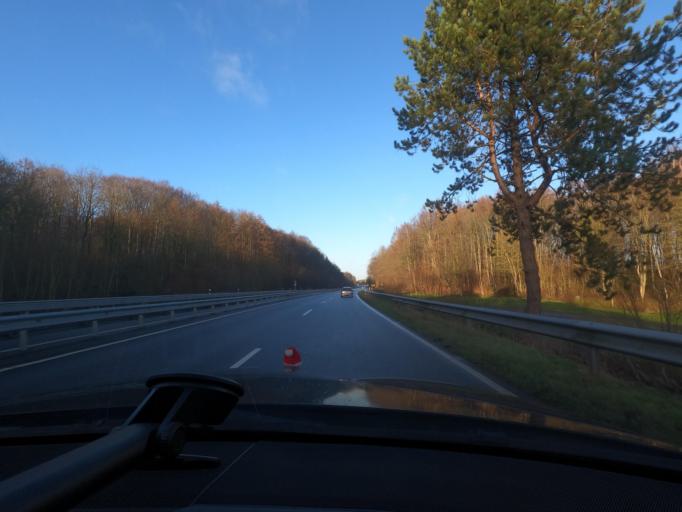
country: DK
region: South Denmark
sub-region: Aabenraa Kommune
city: Krusa
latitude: 54.8262
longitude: 9.4146
